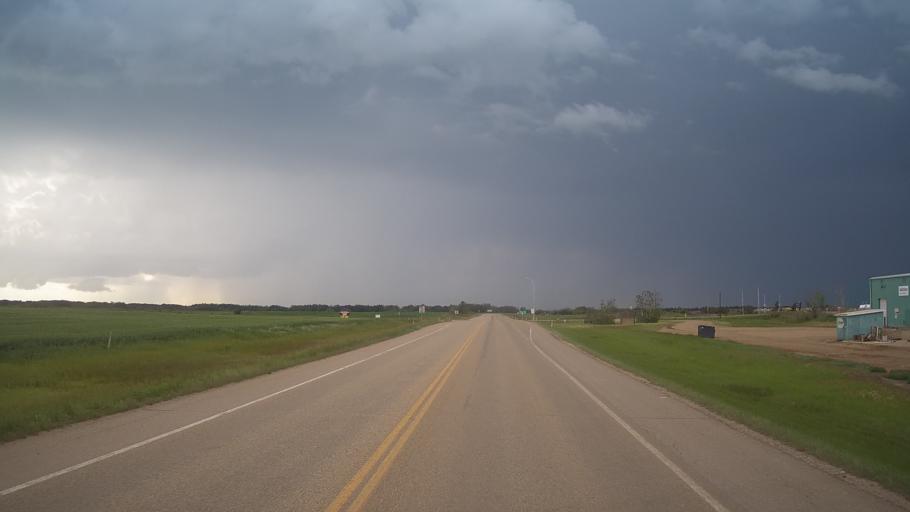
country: CA
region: Alberta
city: Tofield
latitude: 53.2891
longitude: -112.4376
